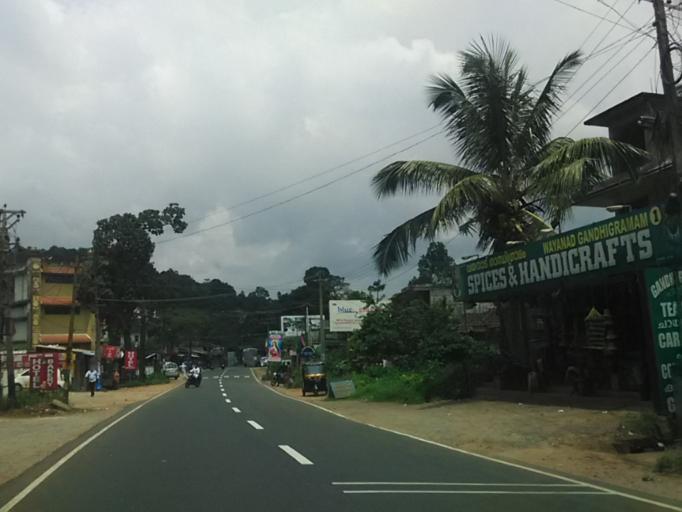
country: IN
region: Kerala
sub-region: Wayanad
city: Kalpetta
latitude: 11.5405
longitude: 76.0370
